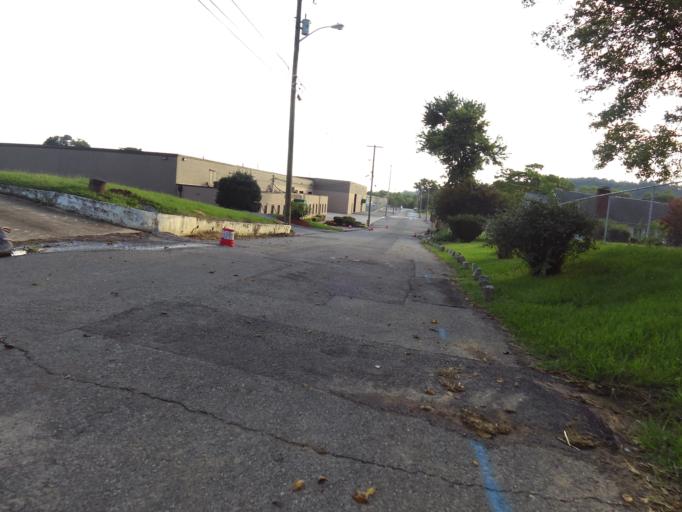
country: US
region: Tennessee
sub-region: Knox County
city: Knoxville
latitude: 35.9954
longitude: -83.9416
